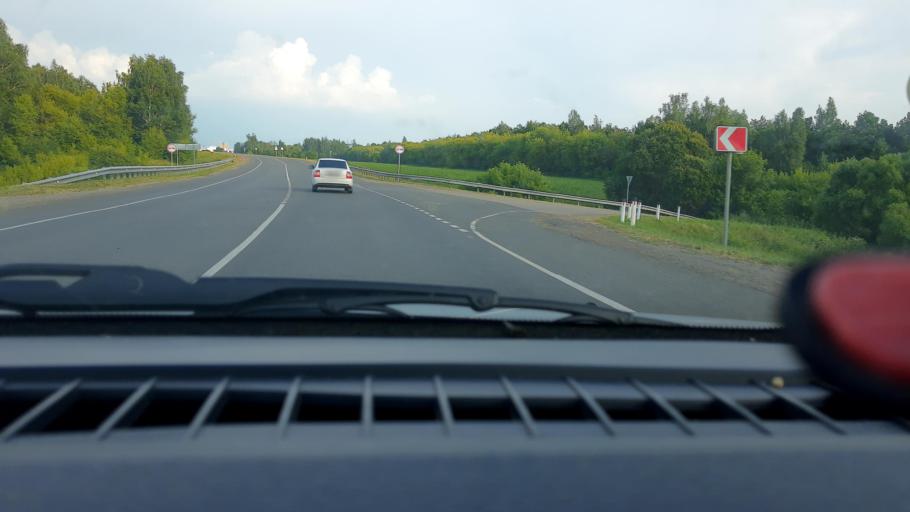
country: RU
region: Nizjnij Novgorod
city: Arzamas
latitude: 55.3172
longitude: 43.8907
